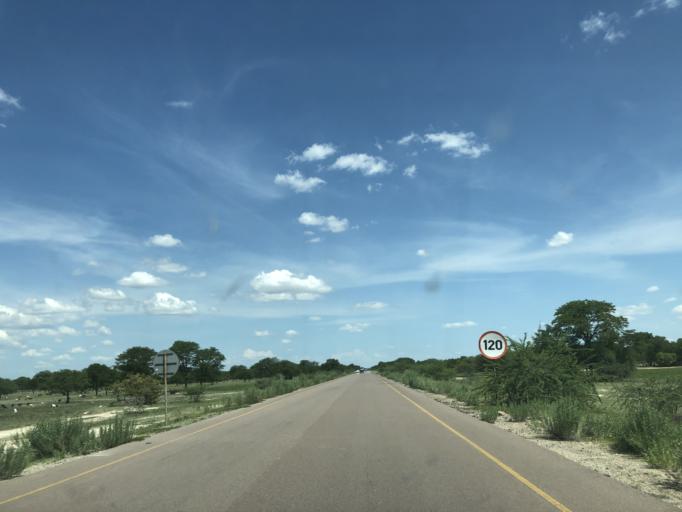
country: AO
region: Cunene
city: Ondjiva
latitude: -16.8094
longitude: 15.4329
